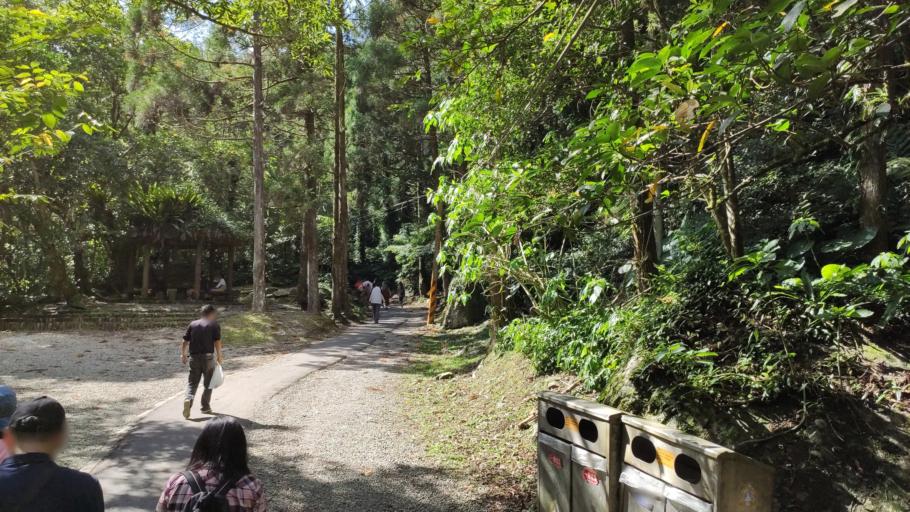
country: TW
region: Taiwan
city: Daxi
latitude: 24.8238
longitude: 121.4496
